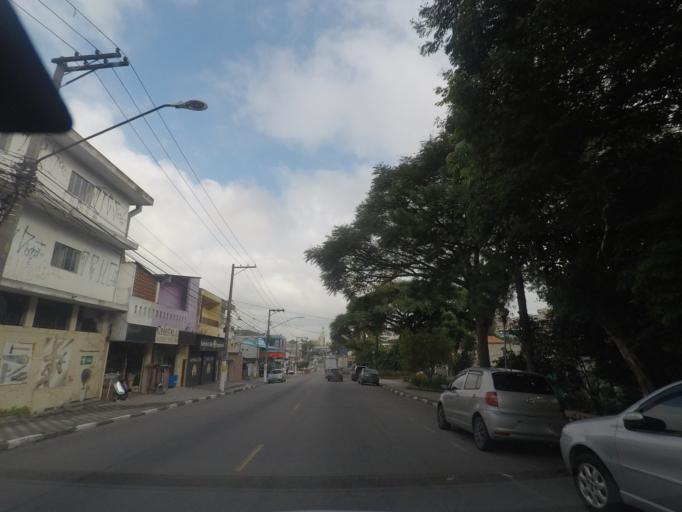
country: BR
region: Sao Paulo
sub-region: Osasco
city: Osasco
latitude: -23.5670
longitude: -46.7802
